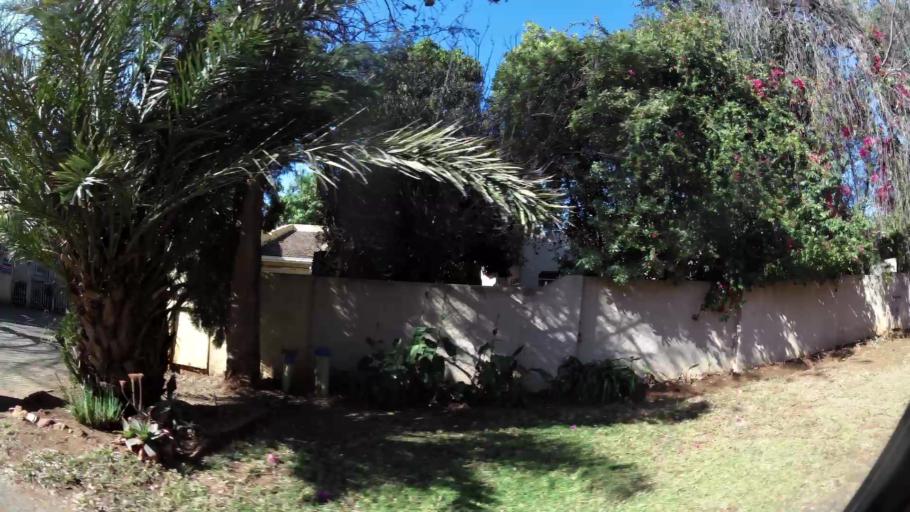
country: ZA
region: Gauteng
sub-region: City of Johannesburg Metropolitan Municipality
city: Roodepoort
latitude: -26.1226
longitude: 27.9687
